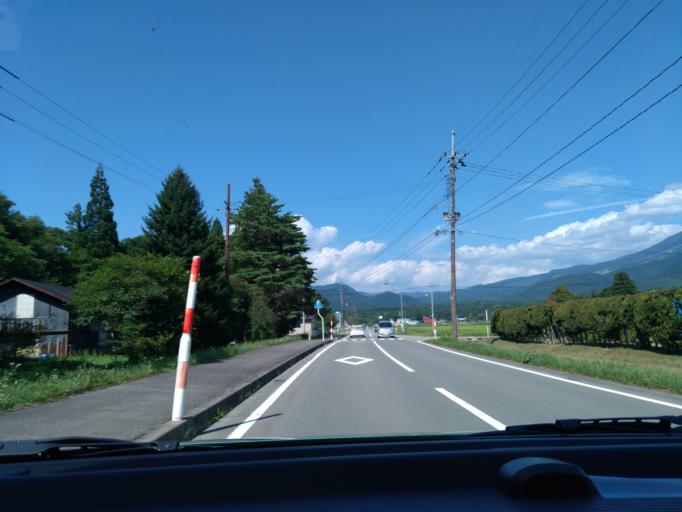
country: JP
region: Akita
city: Kakunodatemachi
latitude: 39.7368
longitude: 140.7088
